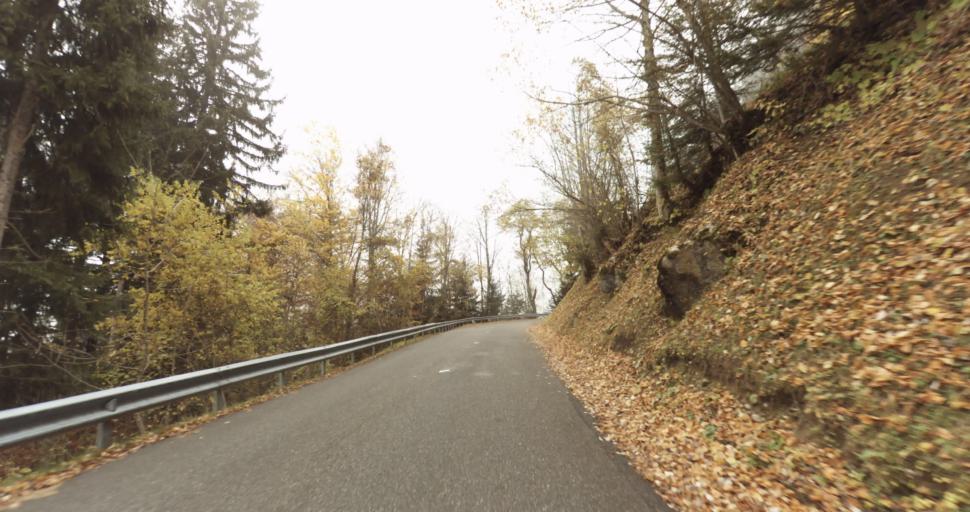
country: FR
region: Rhone-Alpes
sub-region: Departement de la Haute-Savoie
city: Thorens-Glieres
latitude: 45.9664
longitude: 6.2955
